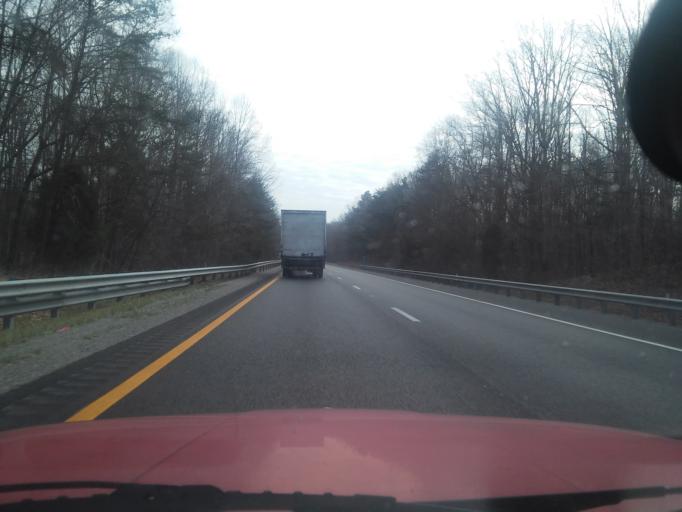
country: US
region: Virginia
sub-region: Goochland County
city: Goochland
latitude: 37.7648
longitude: -77.8693
